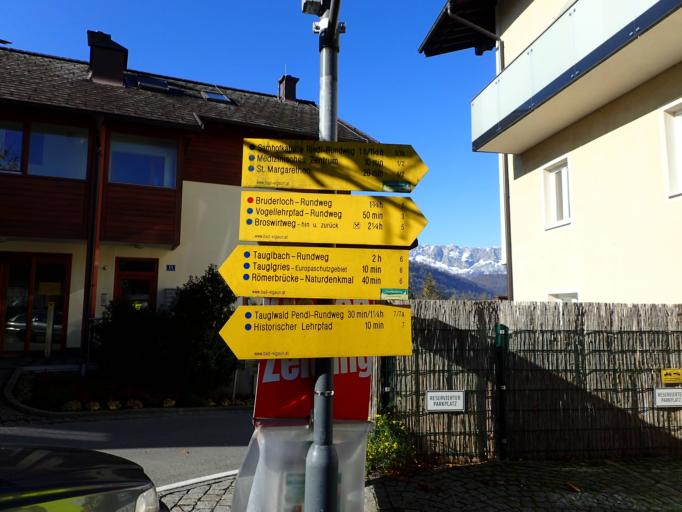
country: AT
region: Salzburg
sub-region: Politischer Bezirk Hallein
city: Adnet
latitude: 47.6631
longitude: 13.1318
